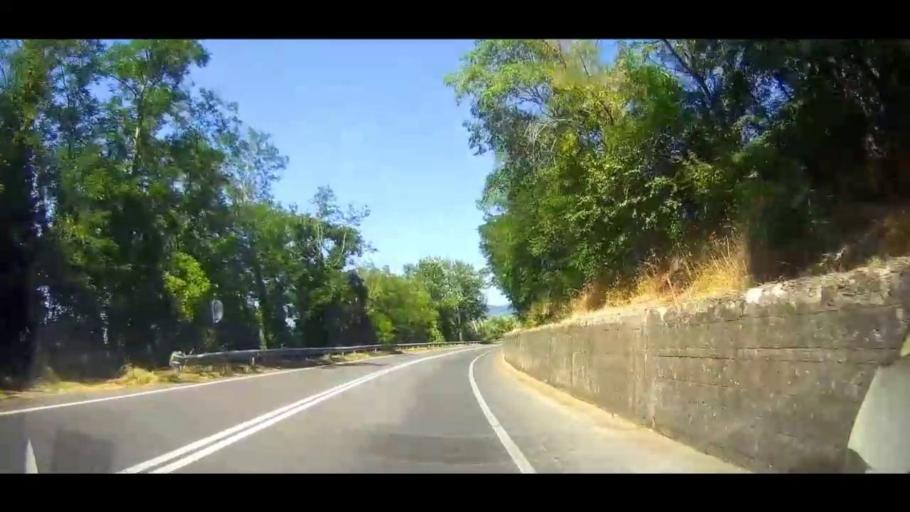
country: IT
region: Calabria
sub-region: Provincia di Cosenza
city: Zumpano
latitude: 39.2956
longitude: 16.2793
